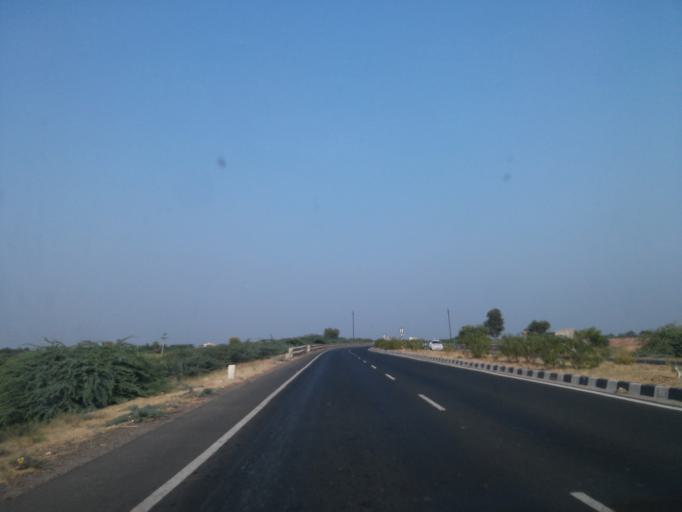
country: IN
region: Gujarat
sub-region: Surendranagar
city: Lakhtar
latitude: 23.0589
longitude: 71.7247
